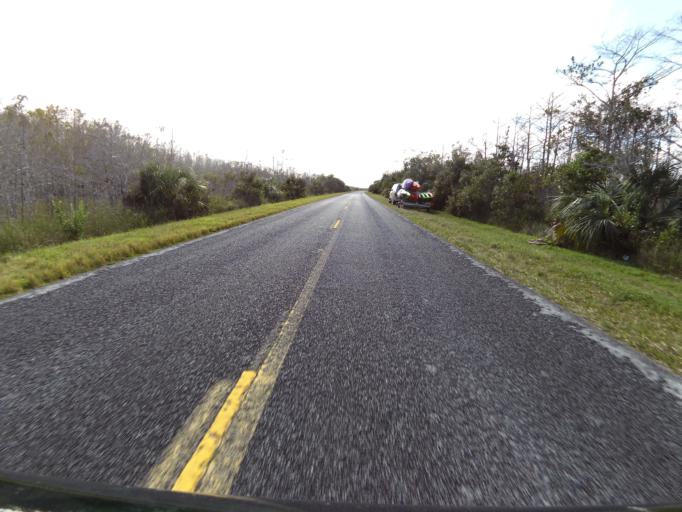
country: US
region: Florida
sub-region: Miami-Dade County
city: Florida City
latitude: 25.4132
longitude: -80.7824
